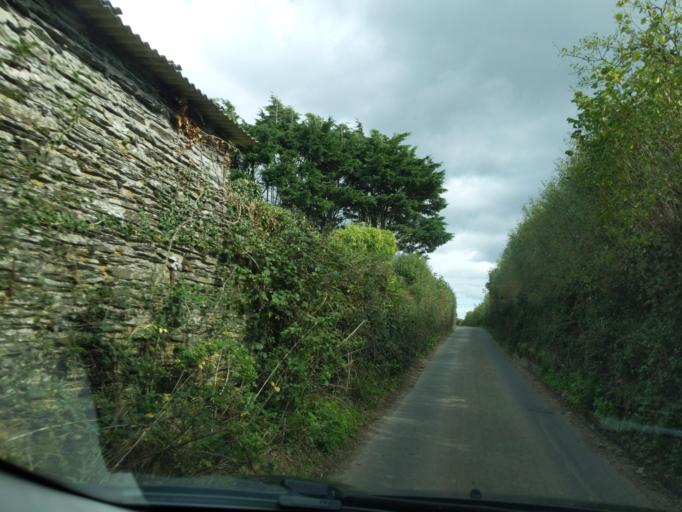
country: GB
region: England
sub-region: Plymouth
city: Plymstock
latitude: 50.3430
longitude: -4.0883
